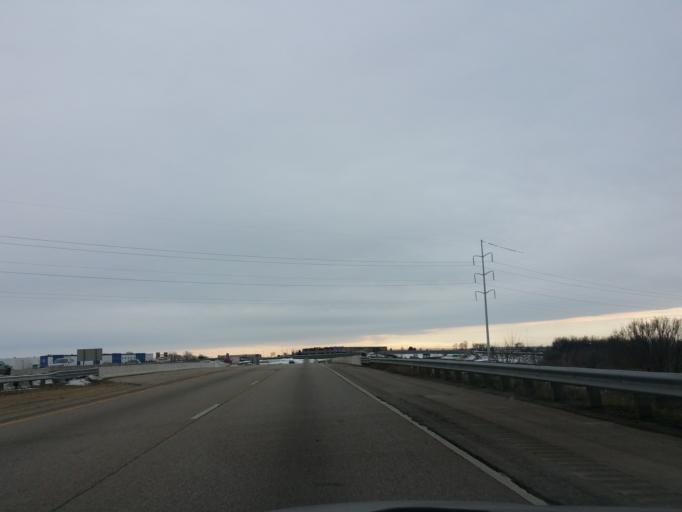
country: US
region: Wisconsin
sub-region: Rock County
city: Beloit
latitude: 42.5211
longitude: -88.9756
